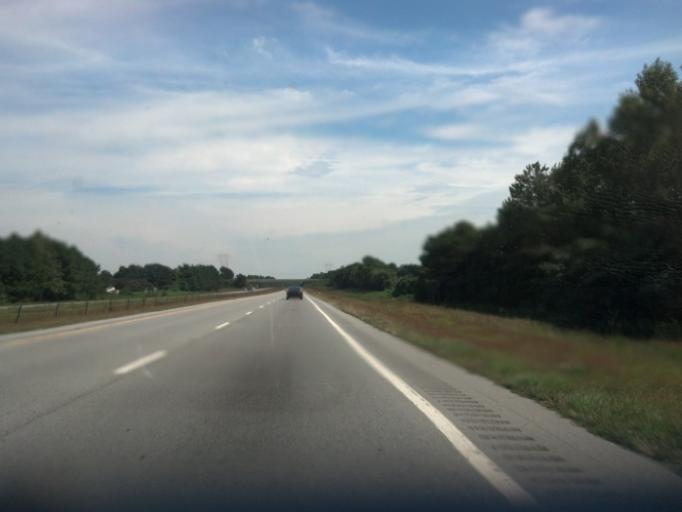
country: US
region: North Carolina
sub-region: Pitt County
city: Farmville
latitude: 35.6003
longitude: -77.5317
